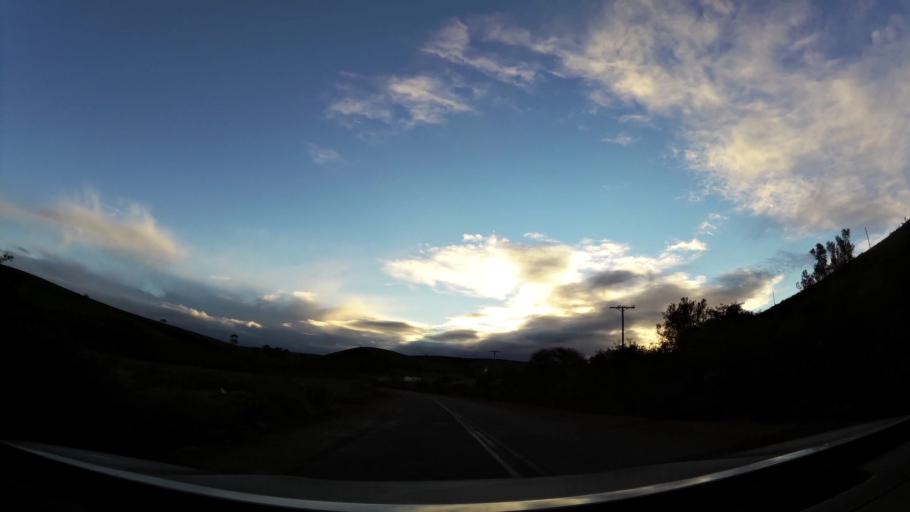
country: ZA
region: Western Cape
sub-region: Eden District Municipality
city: Riversdale
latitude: -34.0553
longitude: 20.8591
